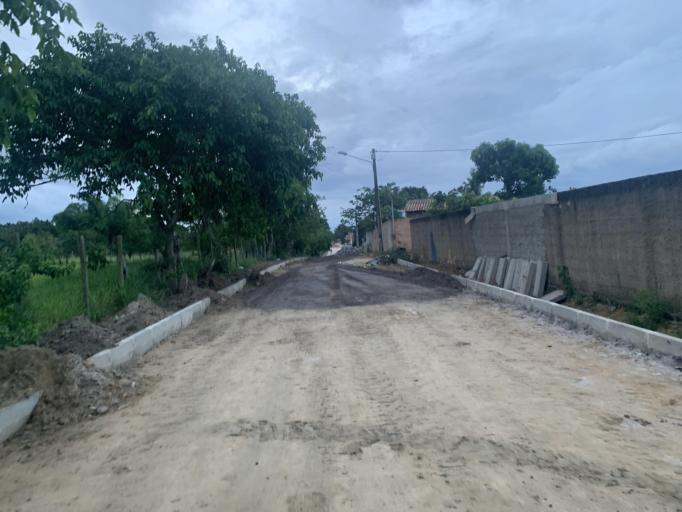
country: BR
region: Bahia
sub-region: Medeiros Neto
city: Medeiros Neto
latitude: -17.3926
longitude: -40.2310
